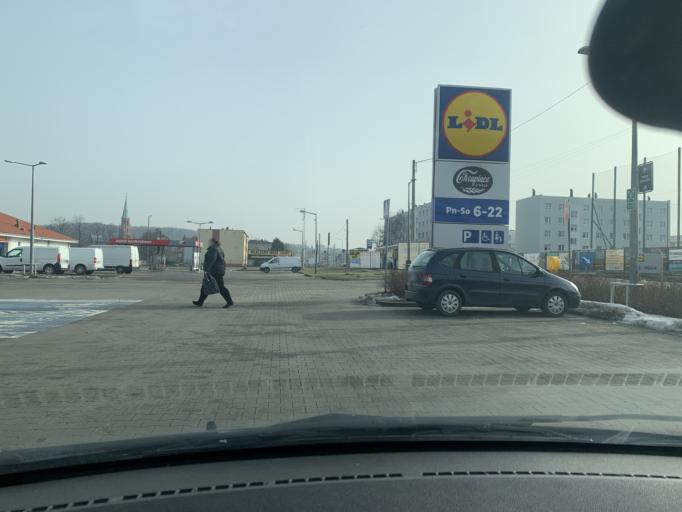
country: PL
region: Silesian Voivodeship
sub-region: Powiat tarnogorski
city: Radzionkow
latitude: 50.4059
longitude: 18.9005
